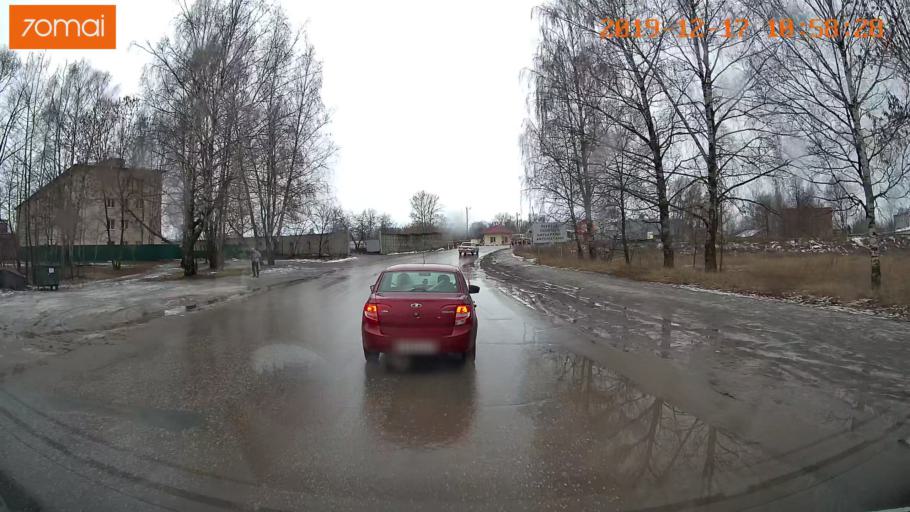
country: RU
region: Vladimir
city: Gus'-Khrustal'nyy
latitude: 55.6227
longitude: 40.6521
